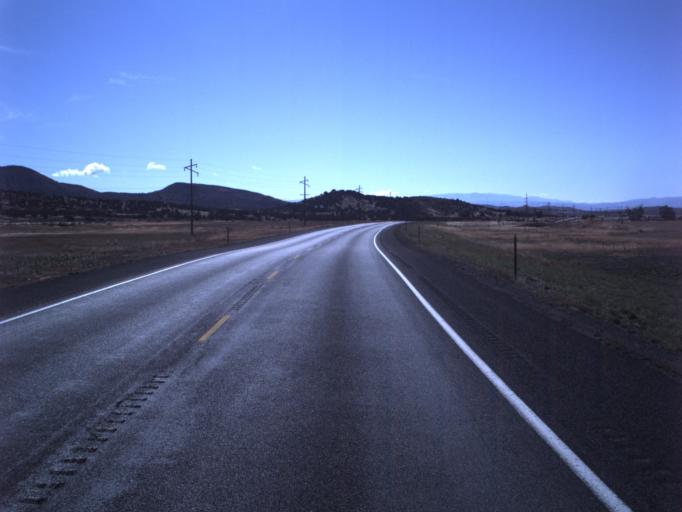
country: US
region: Utah
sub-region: Sanpete County
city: Gunnison
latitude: 39.2372
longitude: -111.8487
